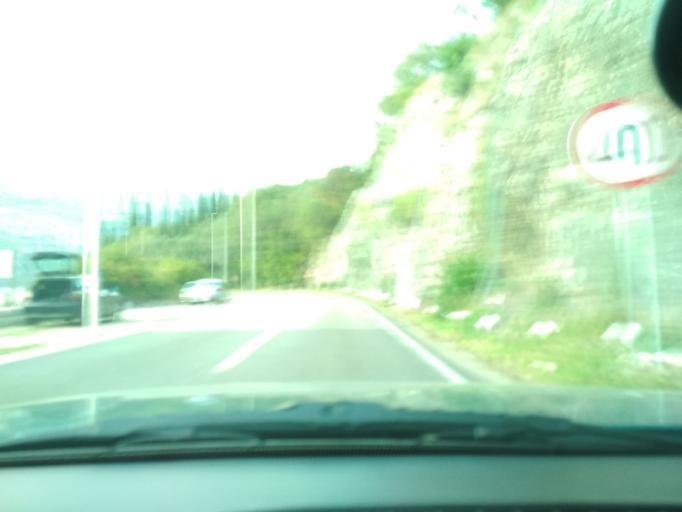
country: ME
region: Kotor
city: Risan
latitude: 42.5000
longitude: 18.6925
